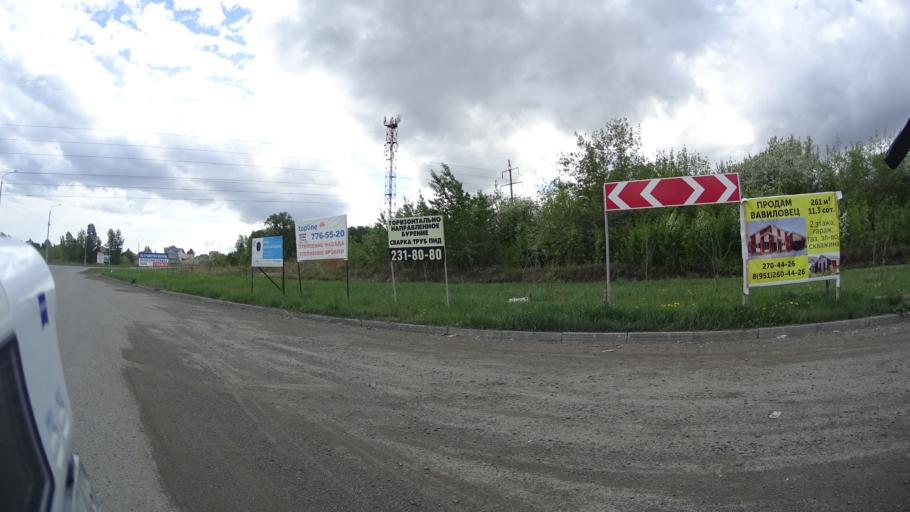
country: RU
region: Chelyabinsk
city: Sargazy
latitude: 55.1590
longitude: 61.2855
